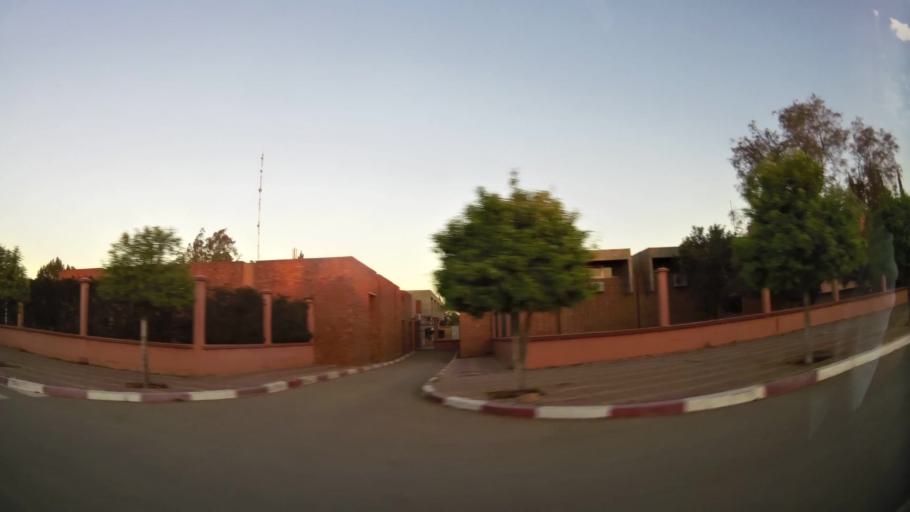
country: MA
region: Marrakech-Tensift-Al Haouz
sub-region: Kelaa-Des-Sraghna
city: Sidi Bou Othmane
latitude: 32.2134
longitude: -7.9292
